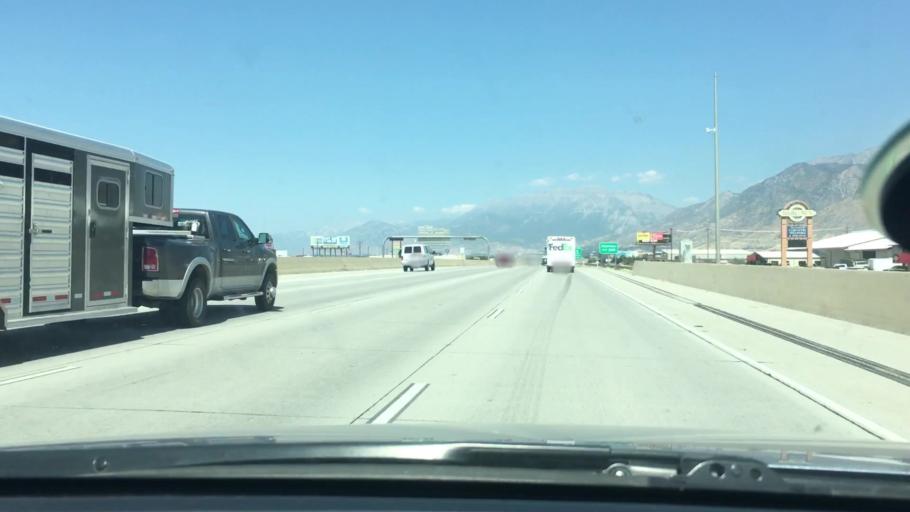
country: US
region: Utah
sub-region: Utah County
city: Spanish Fork
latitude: 40.1473
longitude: -111.6465
